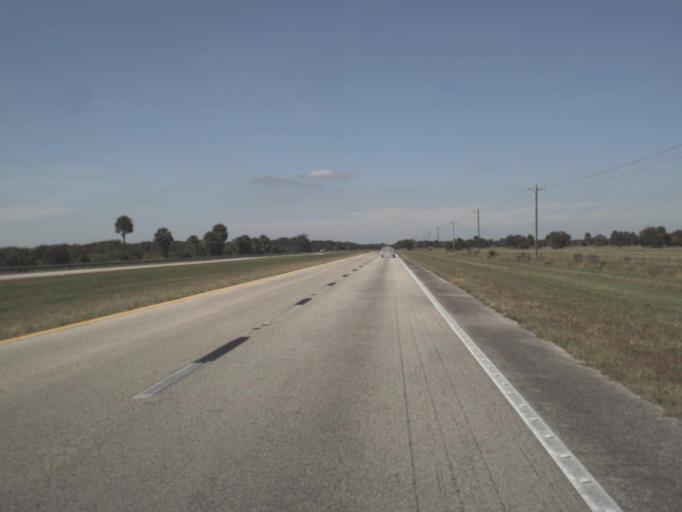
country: US
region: Florida
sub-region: Glades County
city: Moore Haven
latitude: 26.8766
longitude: -81.2241
